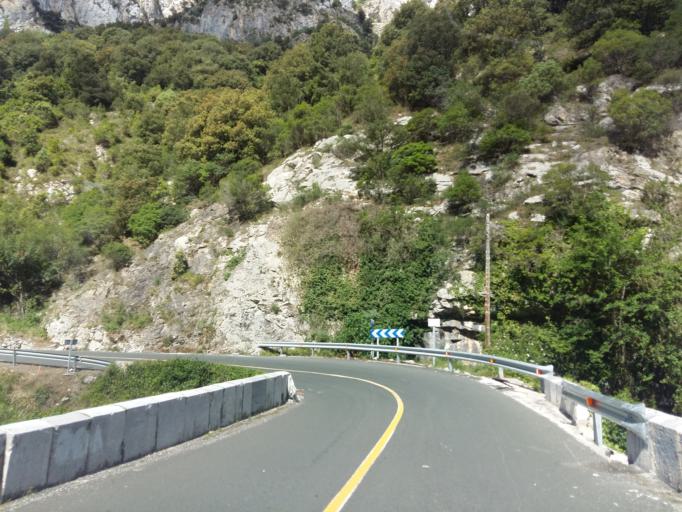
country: ES
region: Cantabria
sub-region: Provincia de Cantabria
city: Potes
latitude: 43.2277
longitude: -4.5831
